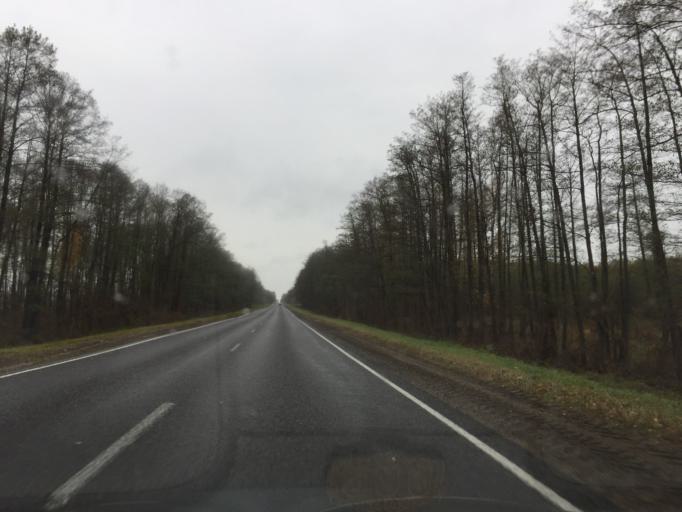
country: BY
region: Mogilev
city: Slawharad
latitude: 53.3544
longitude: 30.8297
